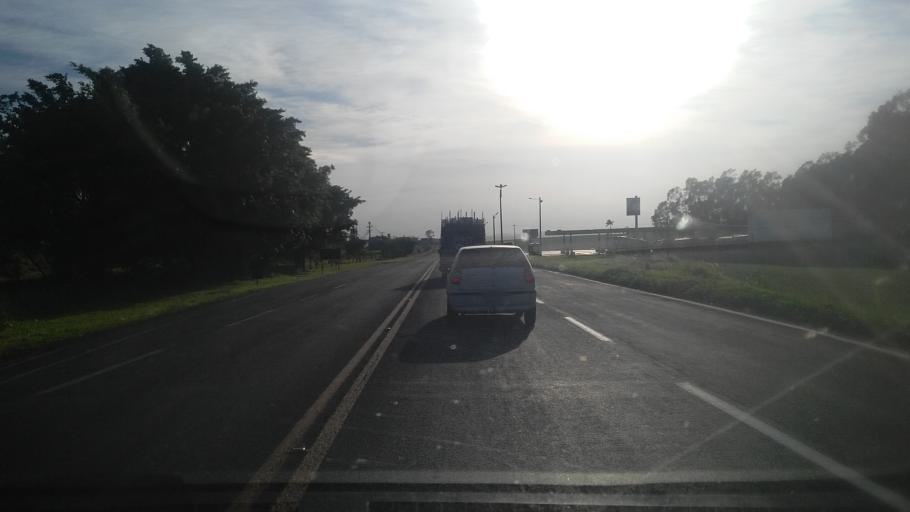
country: BR
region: Parana
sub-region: Bandeirantes
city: Bandeirantes
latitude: -23.1446
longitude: -50.5837
